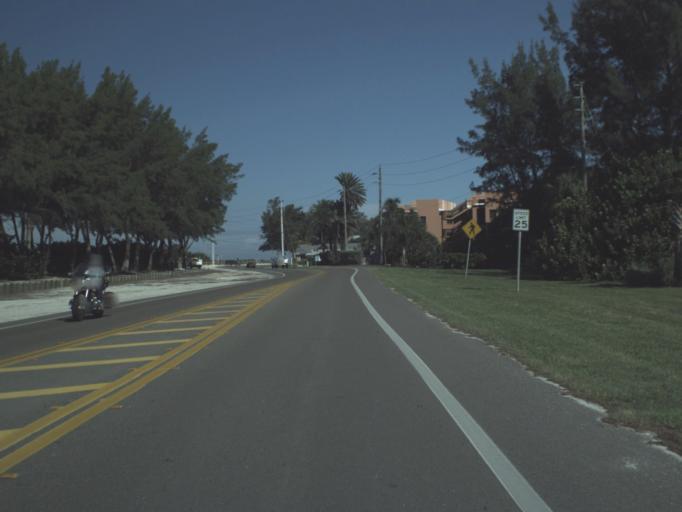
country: US
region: Florida
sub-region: Manatee County
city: Bradenton Beach
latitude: 27.4563
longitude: -82.6947
